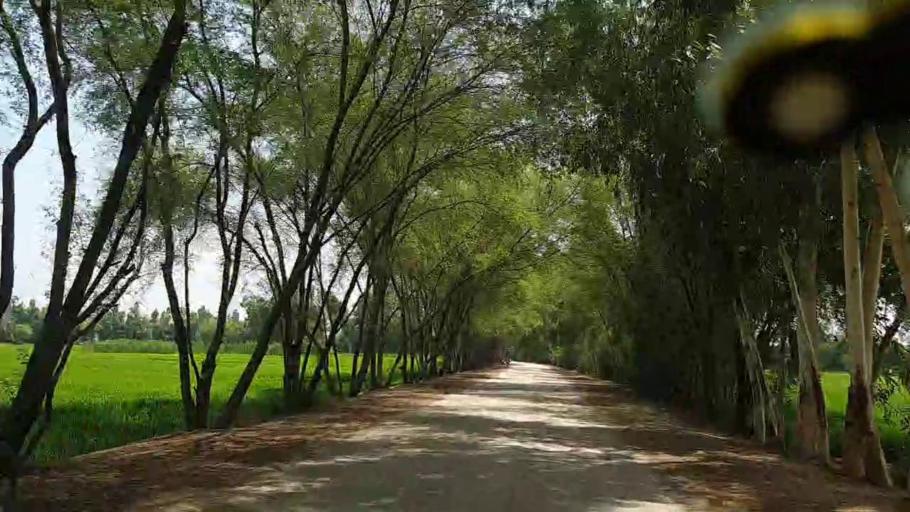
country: PK
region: Sindh
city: Rustam jo Goth
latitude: 28.1091
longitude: 68.8761
